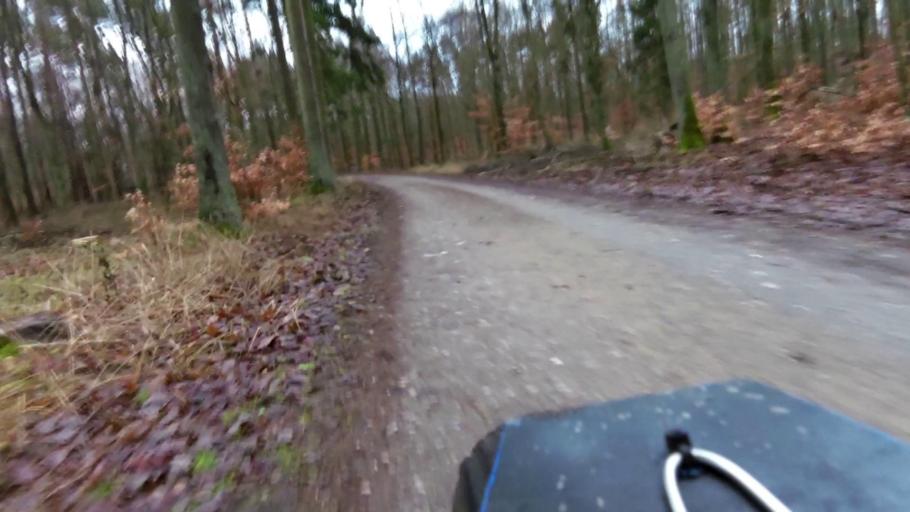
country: PL
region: Lubusz
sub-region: Powiat gorzowski
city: Bogdaniec
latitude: 52.6921
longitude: 15.0069
